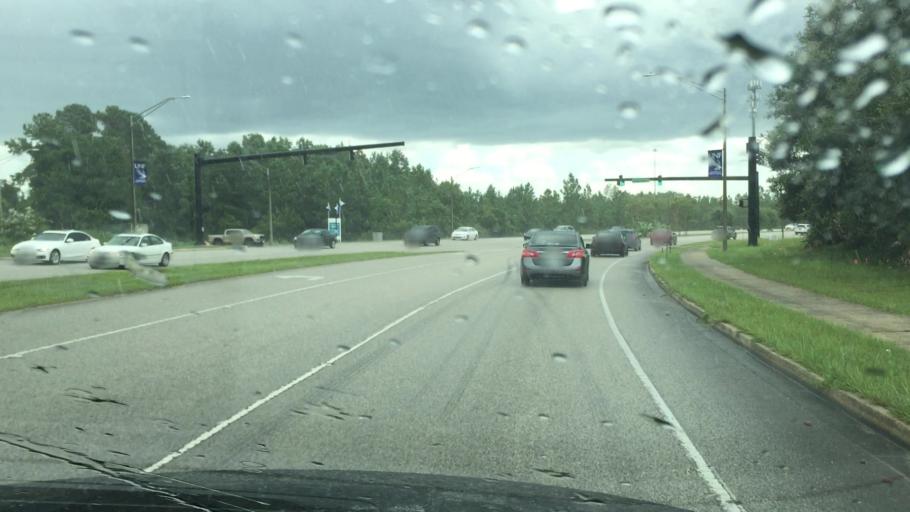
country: US
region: Florida
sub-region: Duval County
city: Jacksonville Beach
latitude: 30.2558
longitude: -81.4982
